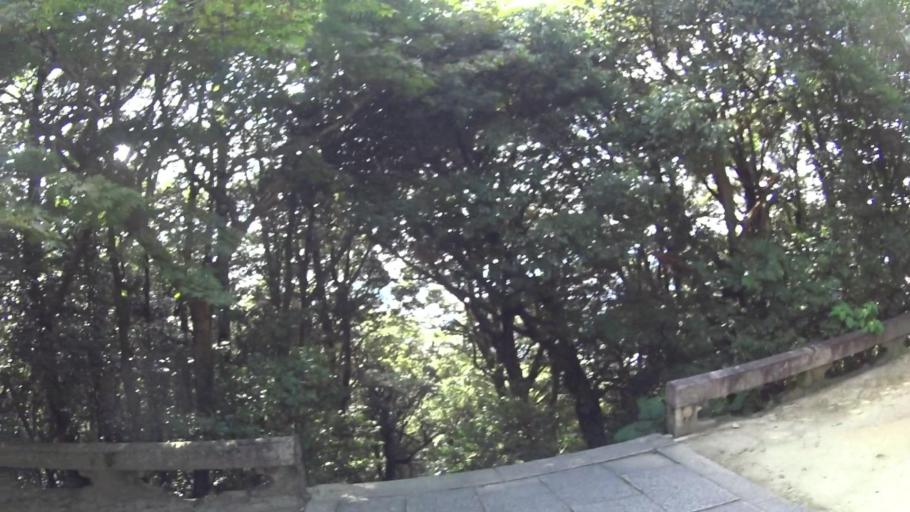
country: RU
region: Rostov
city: Remontnoye
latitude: 46.5014
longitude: 43.7587
